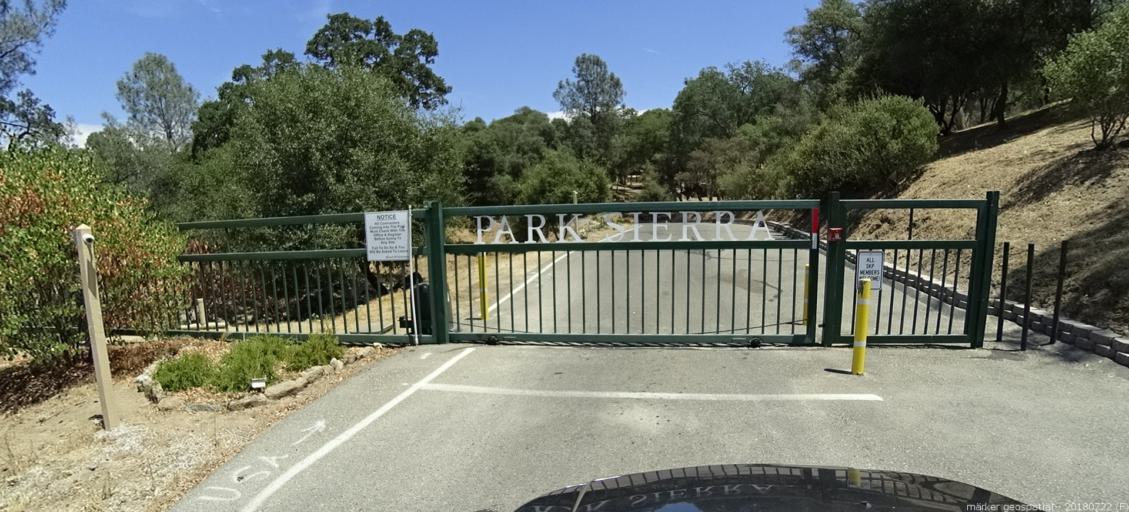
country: US
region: California
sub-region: Madera County
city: Yosemite Lakes
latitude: 37.2052
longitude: -119.7205
